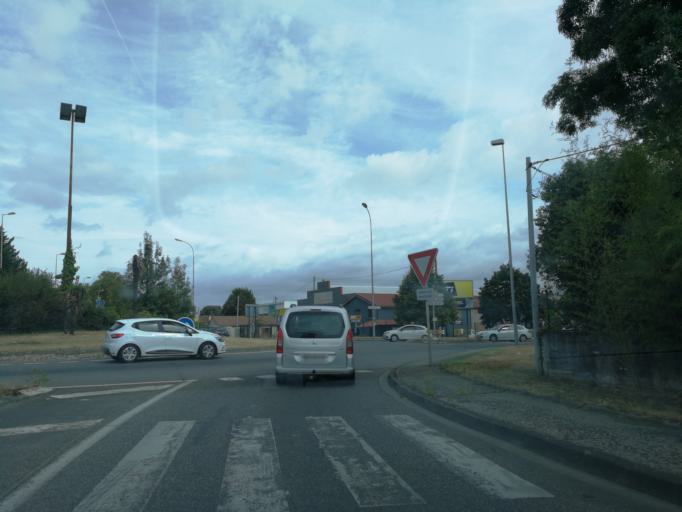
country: FR
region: Midi-Pyrenees
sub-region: Departement de la Haute-Garonne
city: Saint-Alban
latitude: 43.7011
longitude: 1.3971
